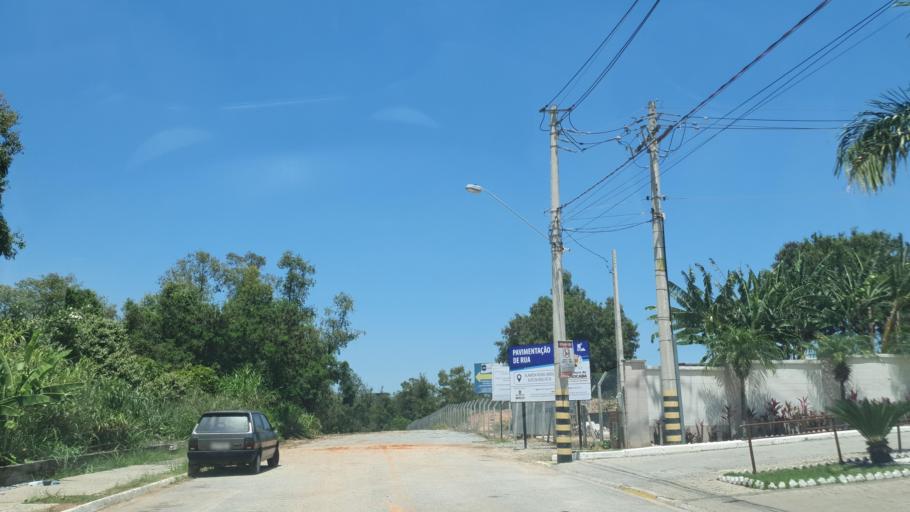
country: BR
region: Sao Paulo
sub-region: Sorocaba
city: Sorocaba
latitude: -23.4722
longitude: -47.4114
